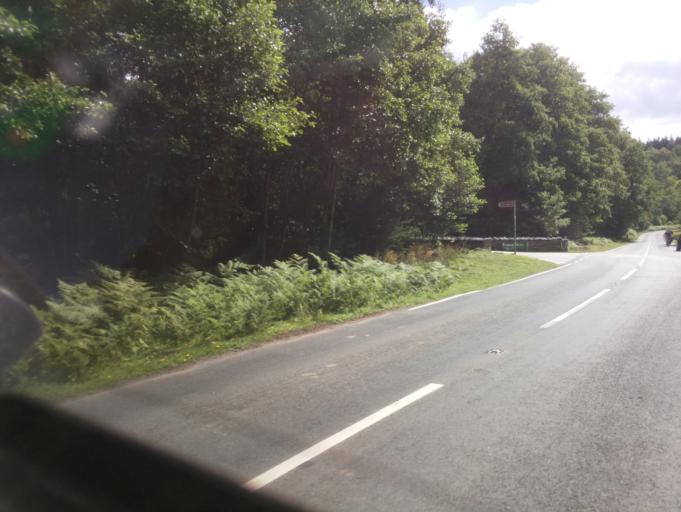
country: GB
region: England
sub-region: Gloucestershire
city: Lydney
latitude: 51.7771
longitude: -2.5271
